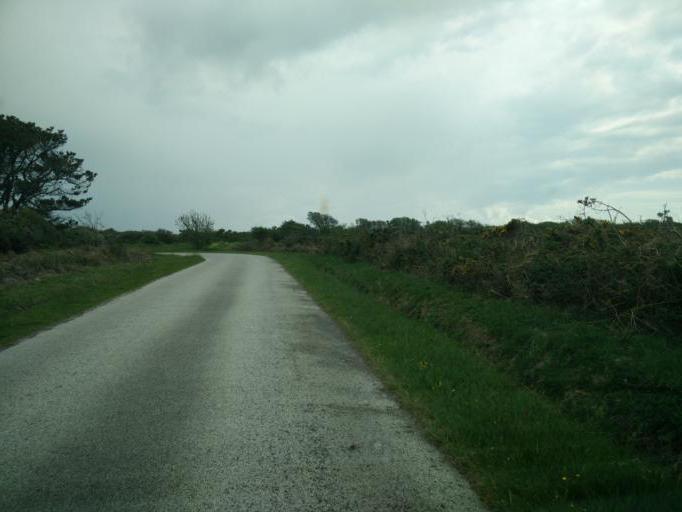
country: FR
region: Brittany
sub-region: Departement du Finistere
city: Roscanvel
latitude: 48.3017
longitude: -4.5652
